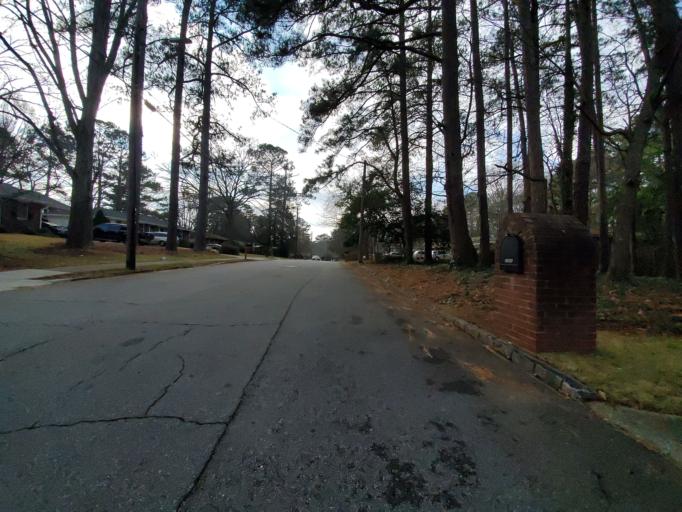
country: US
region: Georgia
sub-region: DeKalb County
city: Scottdale
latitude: 33.8040
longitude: -84.2844
